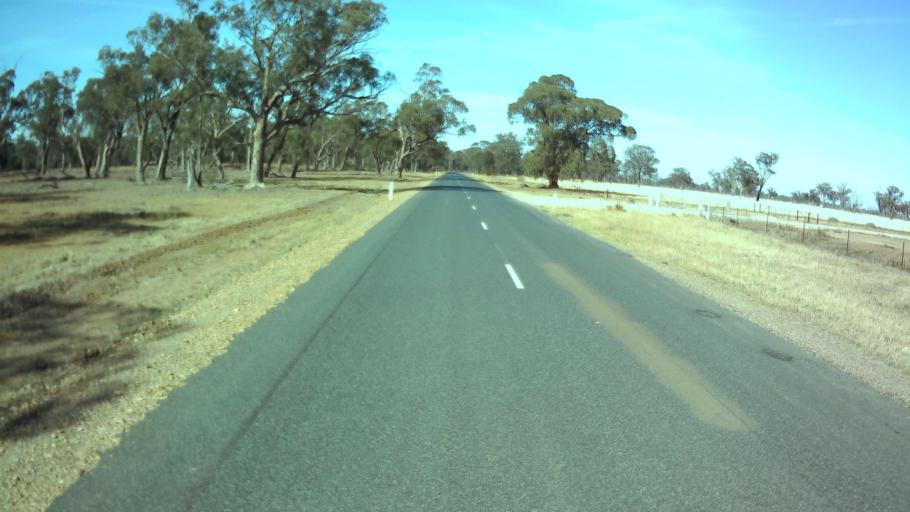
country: AU
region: New South Wales
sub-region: Weddin
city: Grenfell
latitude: -34.1311
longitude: 147.7950
